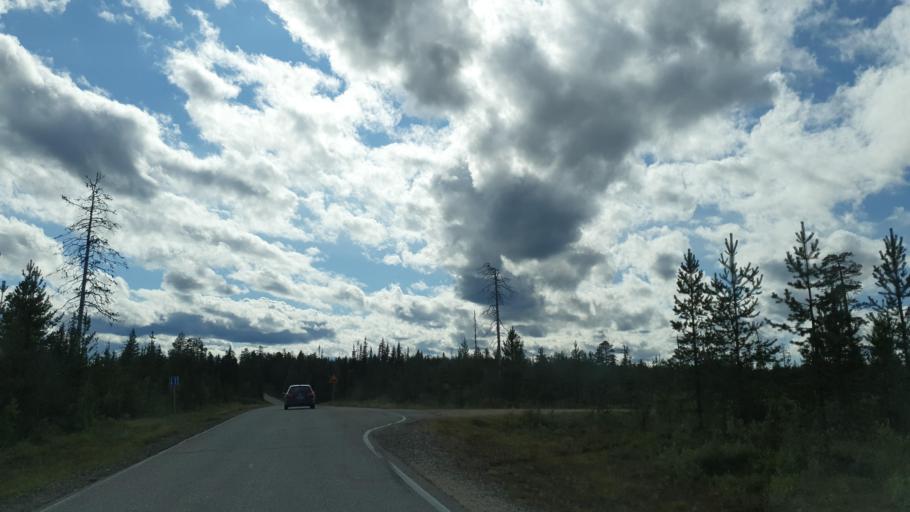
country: FI
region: Lapland
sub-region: Tunturi-Lappi
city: Muonio
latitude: 67.8159
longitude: 24.0682
